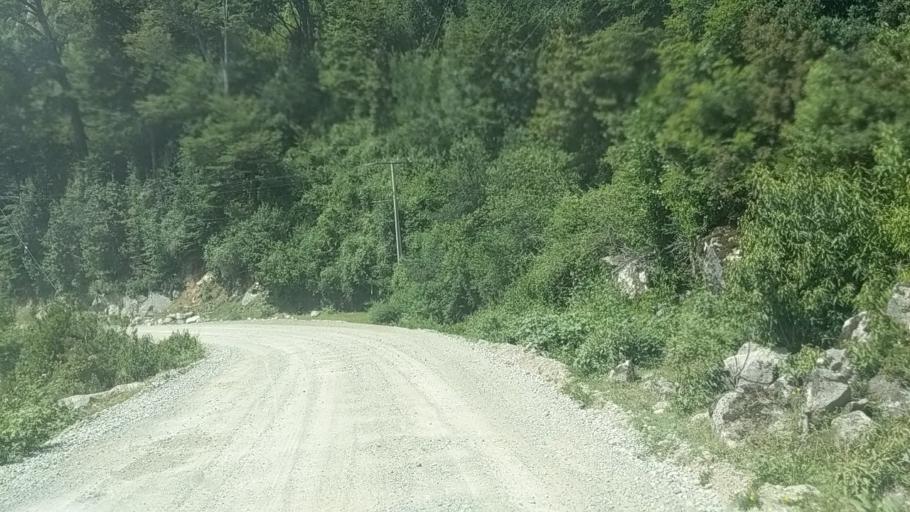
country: CL
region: Los Lagos
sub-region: Provincia de Palena
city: Palena
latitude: -43.4662
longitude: -72.1138
